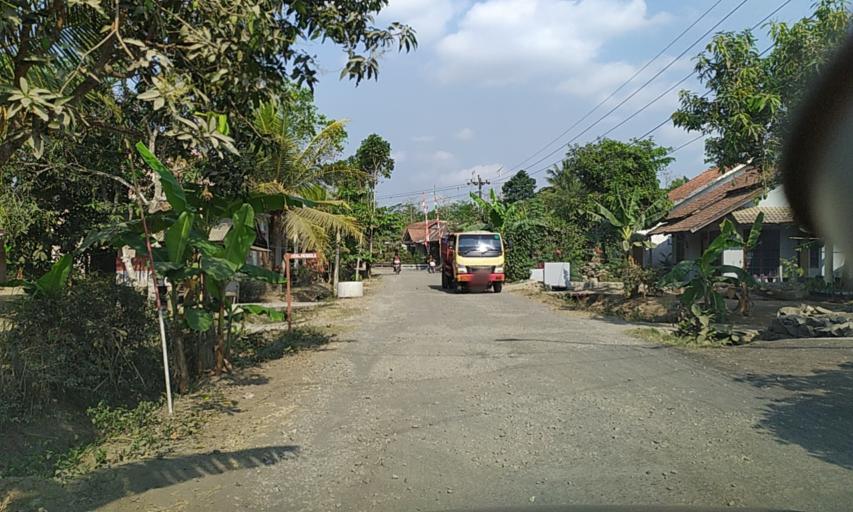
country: ID
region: Central Java
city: Muktisari
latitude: -7.4985
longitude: 108.8931
